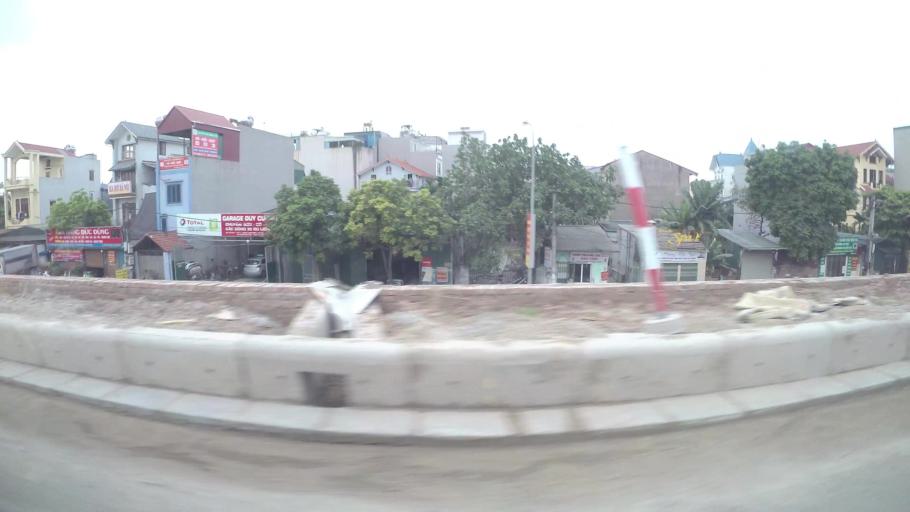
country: VN
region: Ha Noi
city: Trau Quy
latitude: 21.0216
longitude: 105.8944
